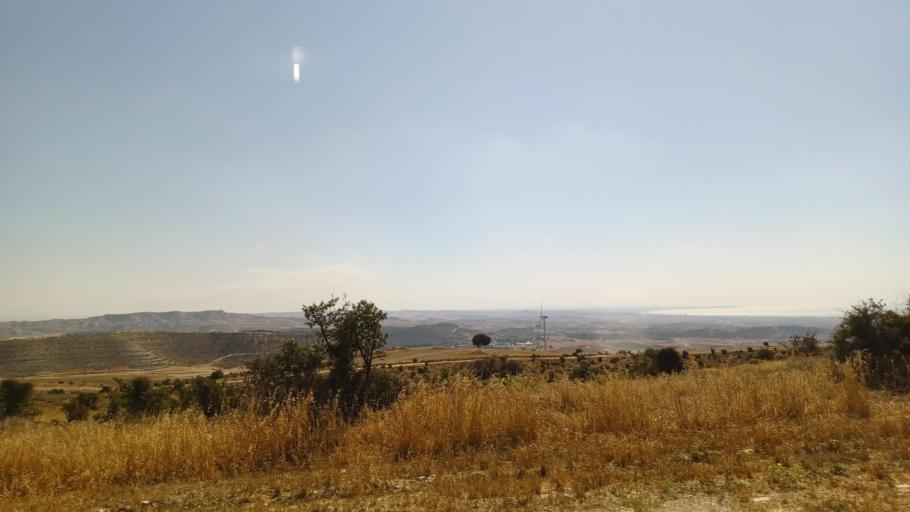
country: CY
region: Larnaka
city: Psevdas
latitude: 34.9703
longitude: 33.4839
